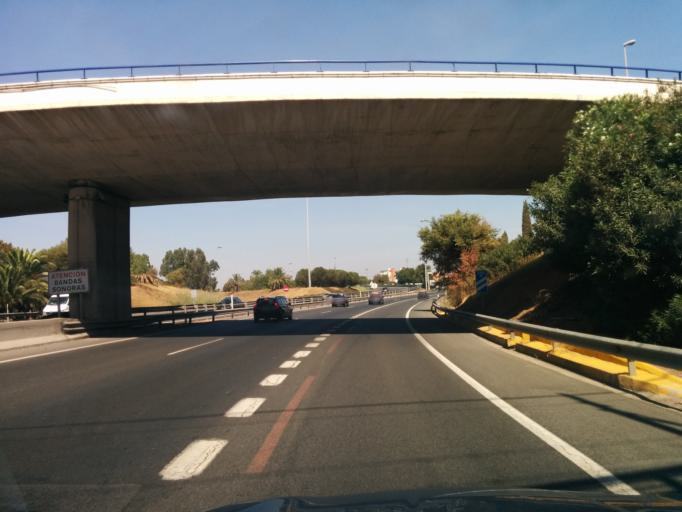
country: ES
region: Andalusia
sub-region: Provincia de Sevilla
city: San Juan de Aznalfarache
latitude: 37.3683
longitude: -6.0142
